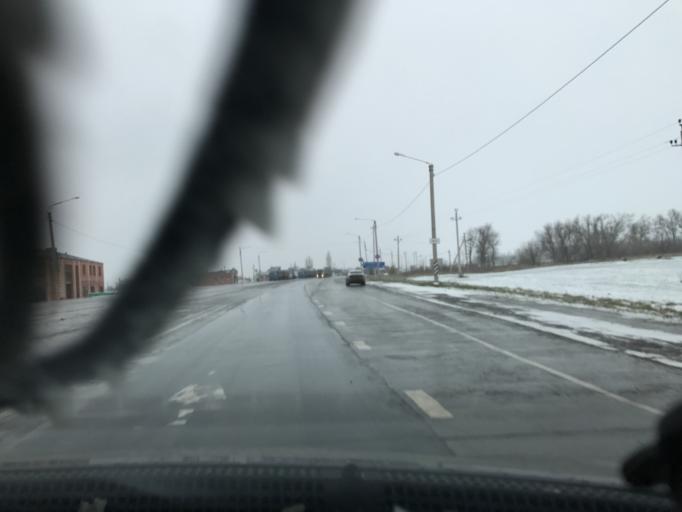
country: RU
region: Rostov
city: Yegorlykskaya
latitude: 46.5526
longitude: 40.6462
